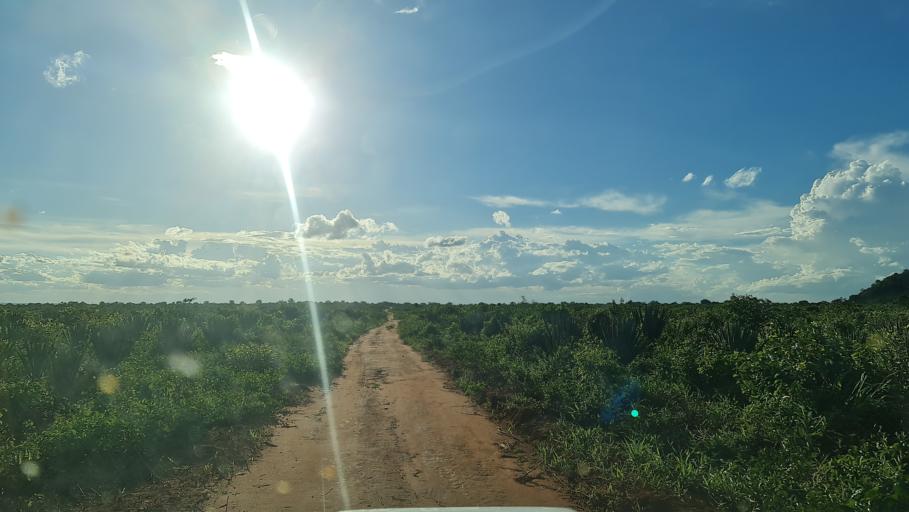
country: MZ
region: Nampula
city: Ilha de Mocambique
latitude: -14.9523
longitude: 40.1802
